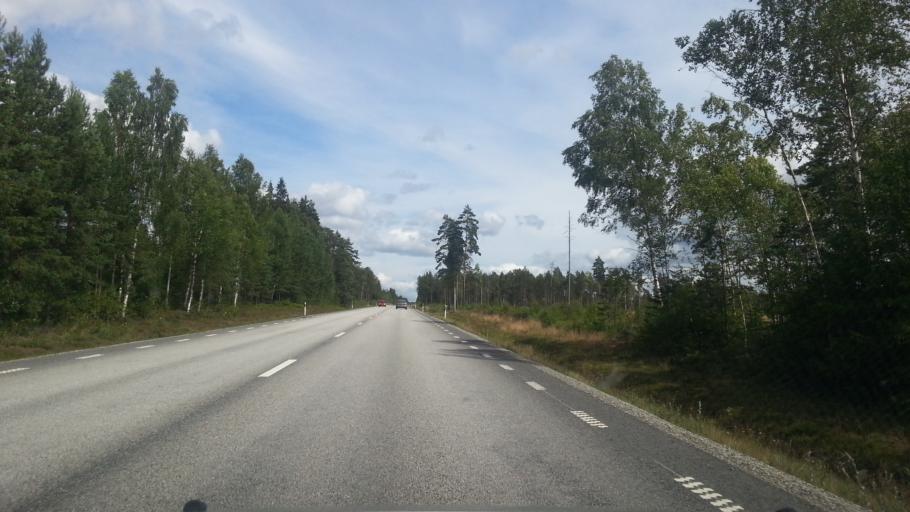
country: SE
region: OErebro
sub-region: Lindesbergs Kommun
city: Lindesberg
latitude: 59.6690
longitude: 15.2831
